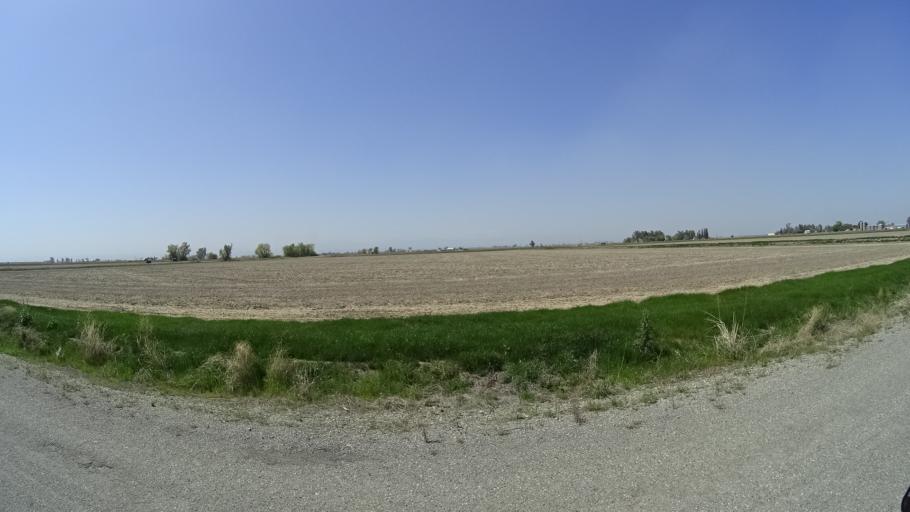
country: US
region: California
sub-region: Glenn County
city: Willows
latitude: 39.5375
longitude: -122.0886
